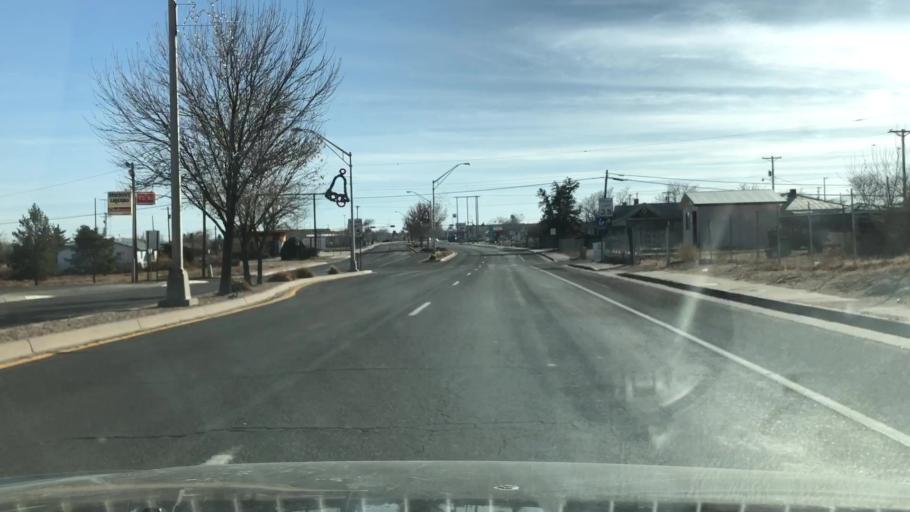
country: US
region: New Mexico
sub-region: Socorro County
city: Socorro
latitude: 34.0556
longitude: -106.8916
